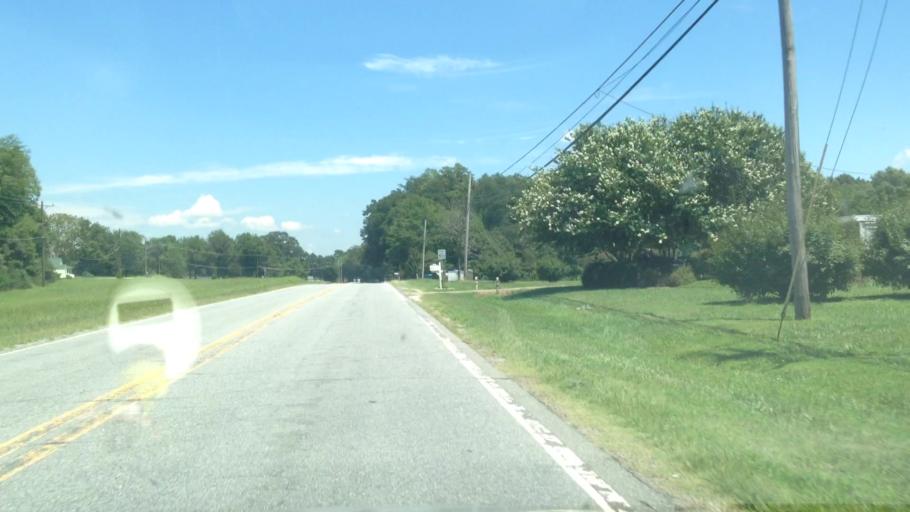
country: US
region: North Carolina
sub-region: Guilford County
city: Stokesdale
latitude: 36.2385
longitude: -79.9396
